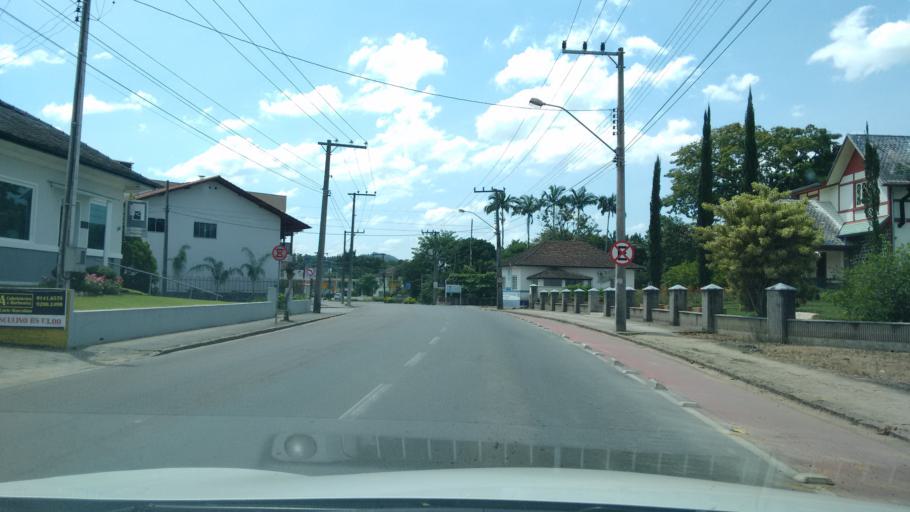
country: BR
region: Santa Catarina
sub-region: Timbo
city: Timbo
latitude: -26.8325
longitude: -49.2638
